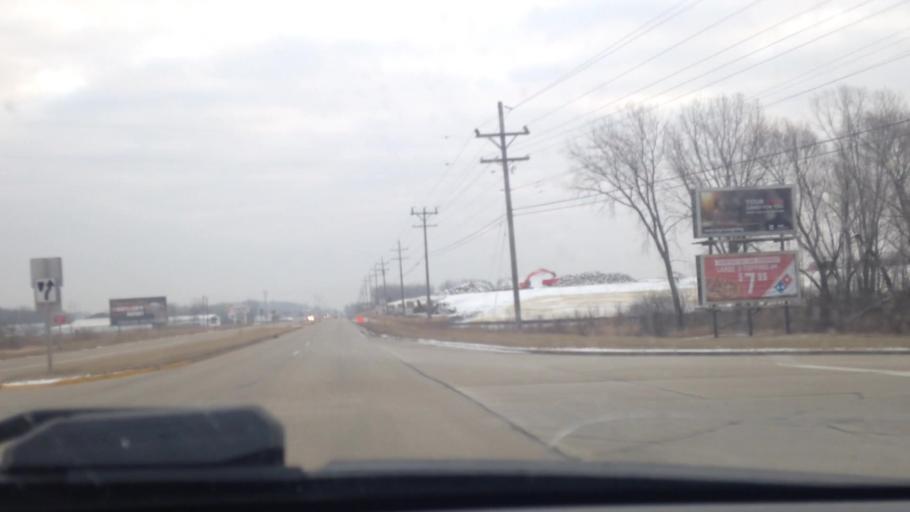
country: US
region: Wisconsin
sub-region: Washington County
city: West Bend
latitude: 43.4273
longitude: -88.2414
